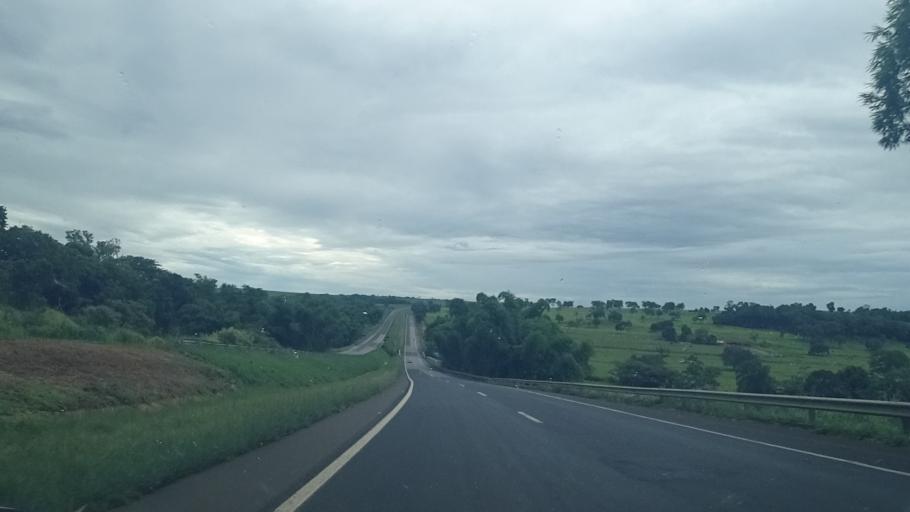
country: BR
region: Goias
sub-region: Goiatuba
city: Goiatuba
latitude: -18.1421
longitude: -49.2885
